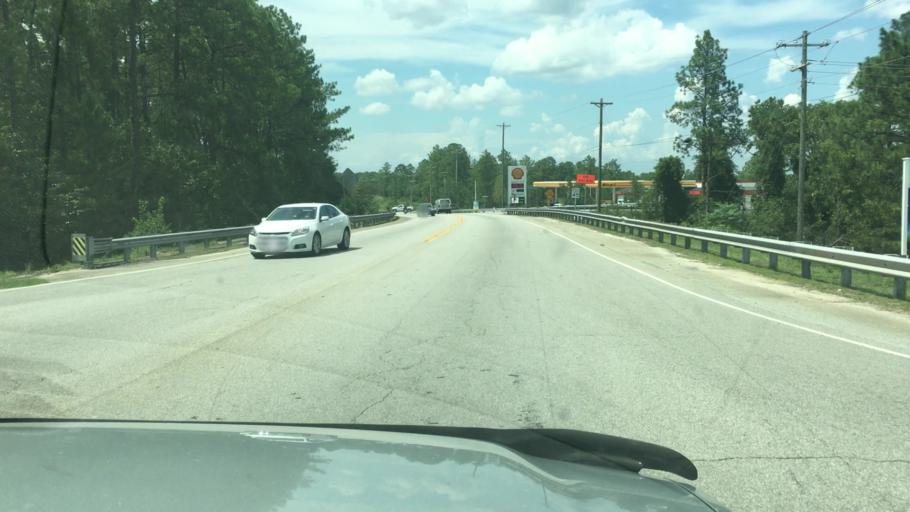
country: US
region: South Carolina
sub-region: Kershaw County
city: Elgin
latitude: 34.1055
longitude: -80.8299
